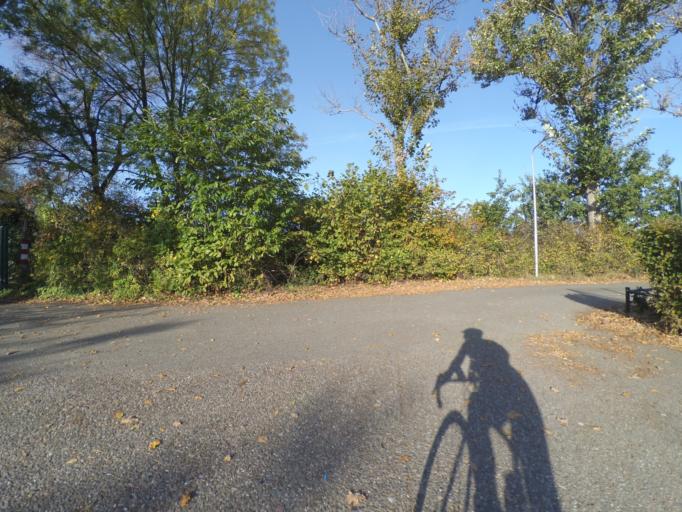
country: NL
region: Utrecht
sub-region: Gemeente Bunnik
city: Bunnik
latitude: 52.0886
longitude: 5.2065
